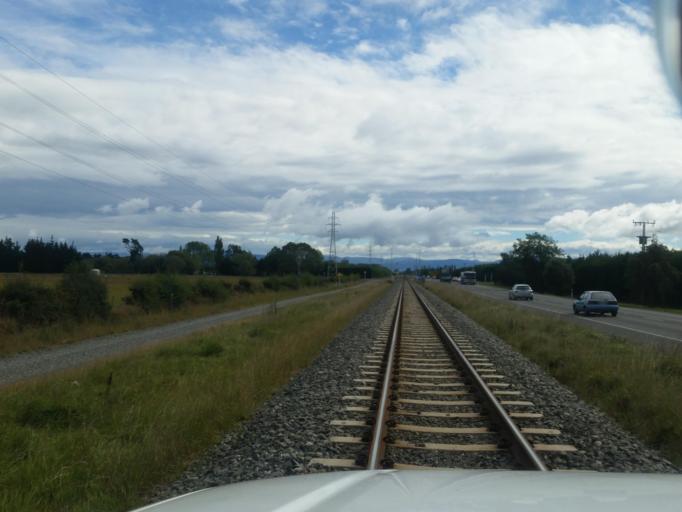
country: NZ
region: Canterbury
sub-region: Waimakariri District
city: Kaiapoi
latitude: -43.3462
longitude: 172.6181
